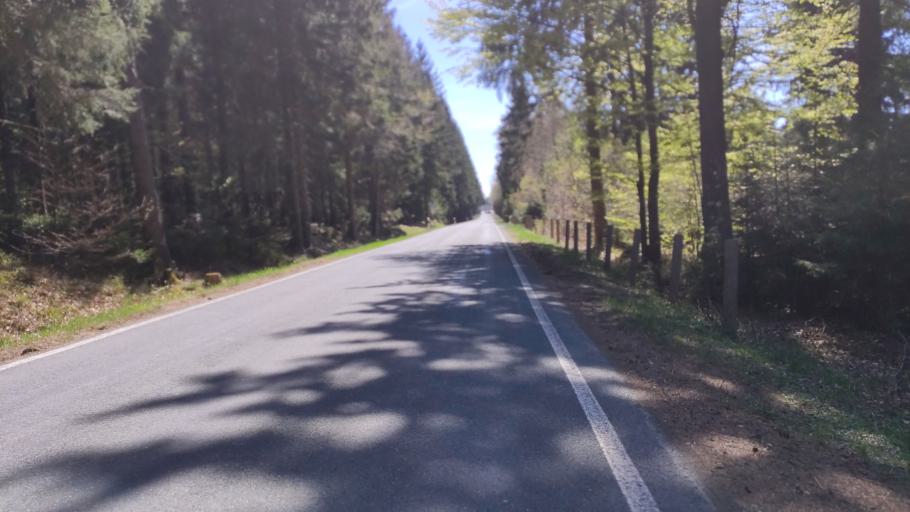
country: DE
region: Bavaria
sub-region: Upper Franconia
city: Tschirn
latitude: 50.4434
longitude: 11.4643
